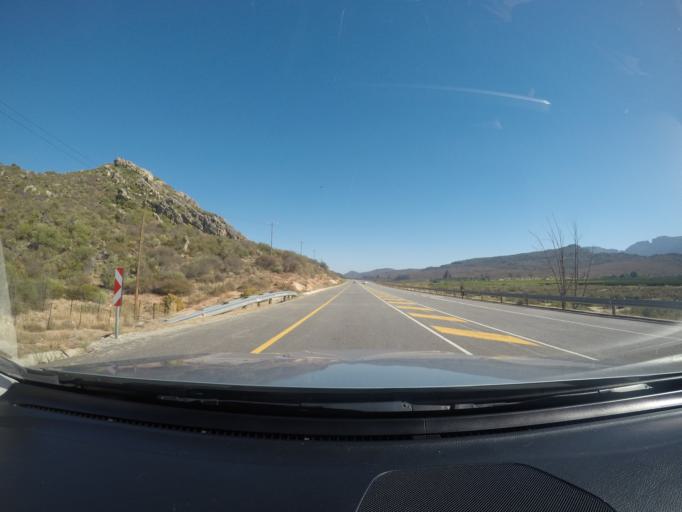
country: ZA
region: Western Cape
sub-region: West Coast District Municipality
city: Clanwilliam
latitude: -32.4458
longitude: 18.9579
